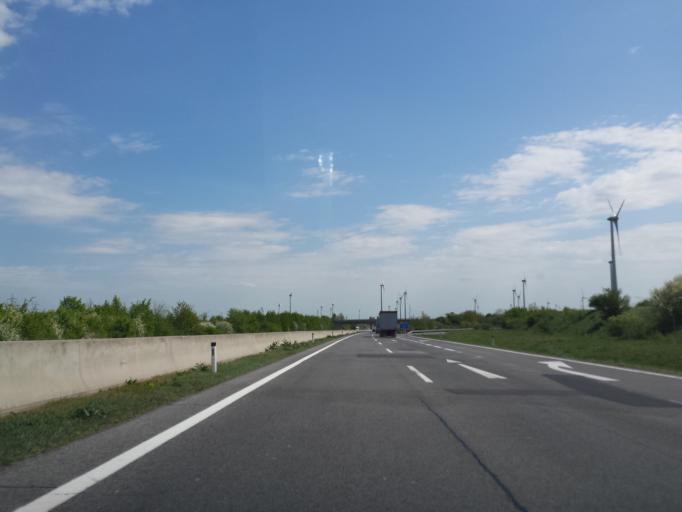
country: AT
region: Burgenland
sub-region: Politischer Bezirk Neusiedl am See
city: Zurndorf
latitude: 47.9337
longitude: 16.9918
